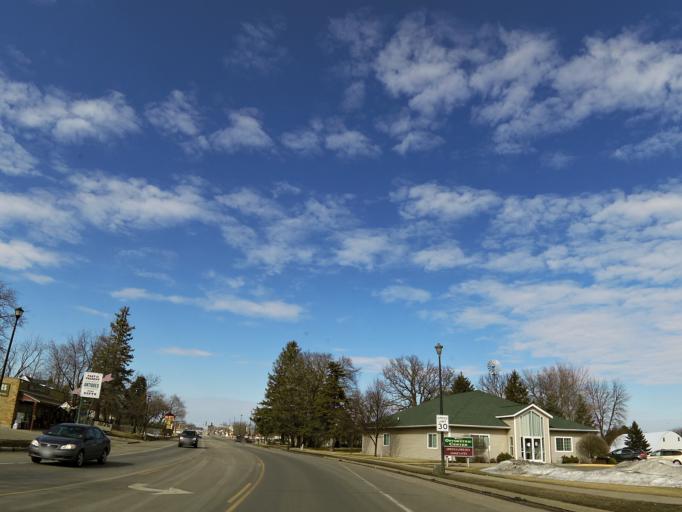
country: US
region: Minnesota
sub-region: Waseca County
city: Waseca
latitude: 44.0881
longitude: -93.5071
